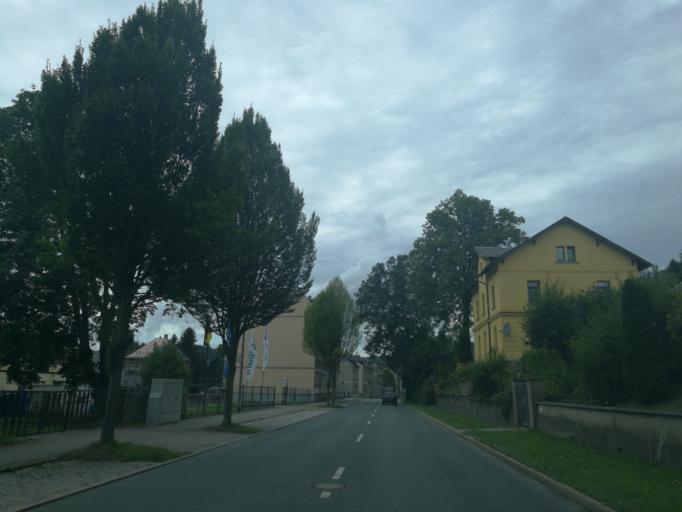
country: DE
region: Saxony
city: Adorf
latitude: 50.3191
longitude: 12.2661
